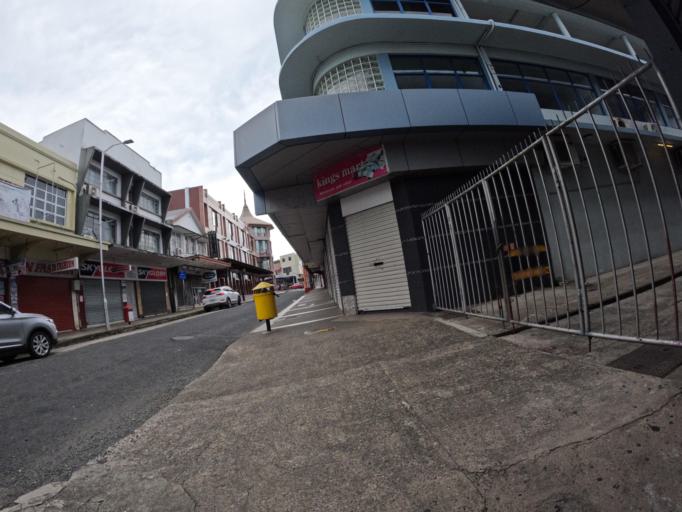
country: FJ
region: Central
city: Suva
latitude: -18.1383
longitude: 178.4263
